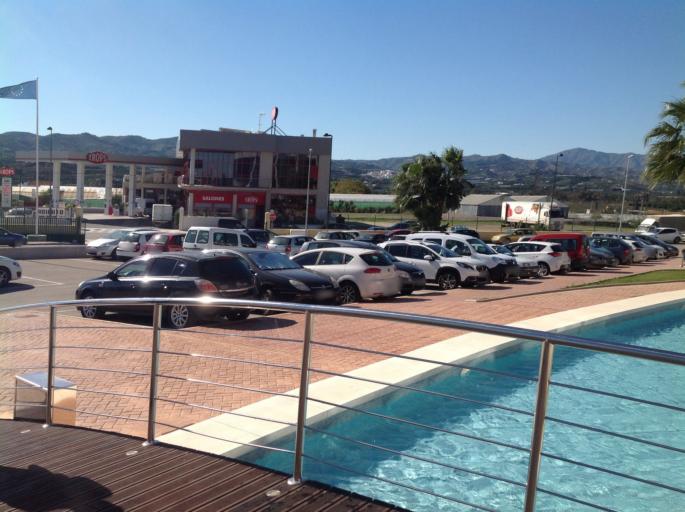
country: ES
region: Andalusia
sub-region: Provincia de Malaga
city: Velez-Malaga
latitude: 36.7990
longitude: -4.1172
